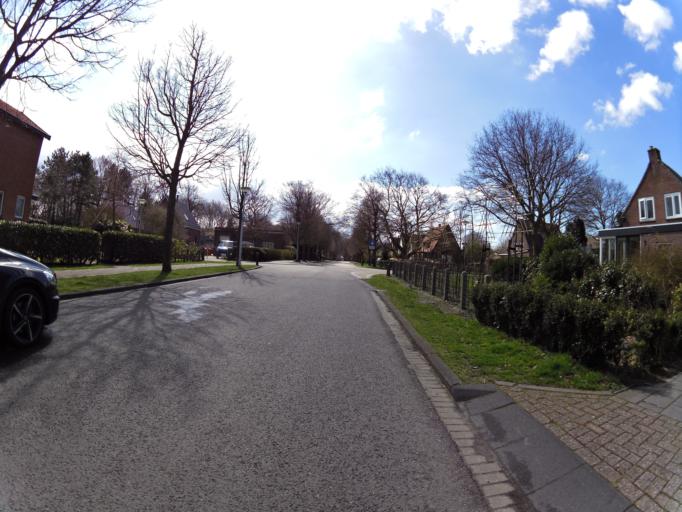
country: NL
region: South Holland
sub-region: Gemeente Brielle
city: Brielle
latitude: 51.9074
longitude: 4.0939
